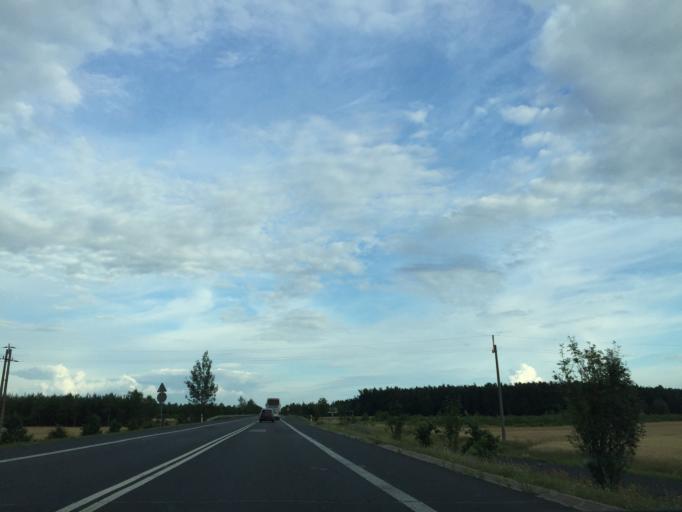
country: PL
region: Lublin Voivodeship
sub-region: Powiat lubartowski
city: Lubartow
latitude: 51.4504
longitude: 22.5799
